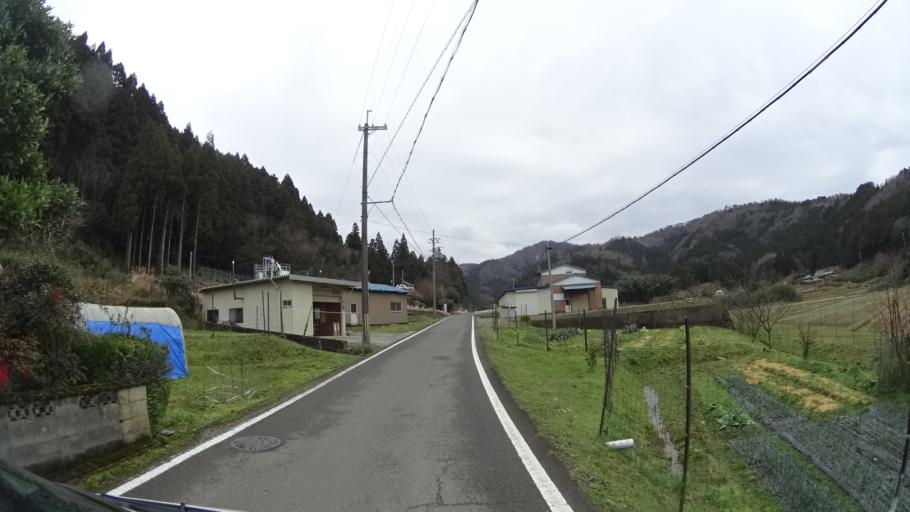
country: JP
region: Kyoto
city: Ayabe
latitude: 35.3325
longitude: 135.3501
